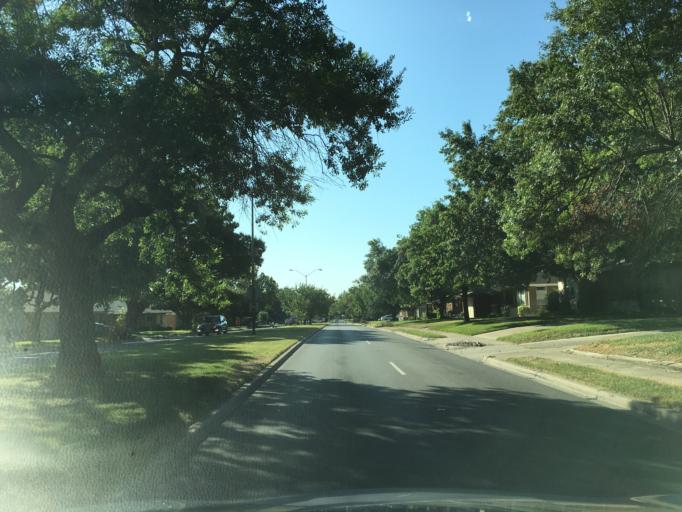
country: US
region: Texas
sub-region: Dallas County
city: Highland Park
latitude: 32.8604
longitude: -96.7093
